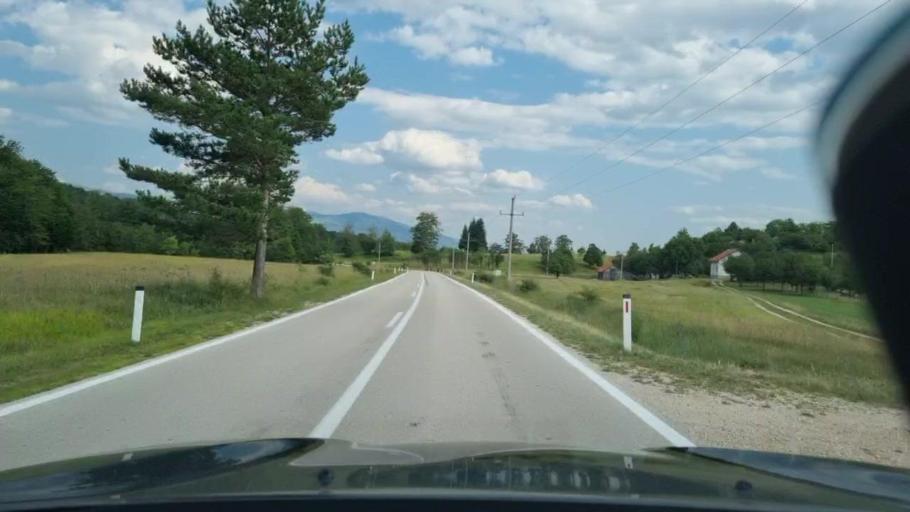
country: BA
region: Federation of Bosnia and Herzegovina
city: Bosansko Grahovo
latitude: 44.1117
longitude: 16.5420
